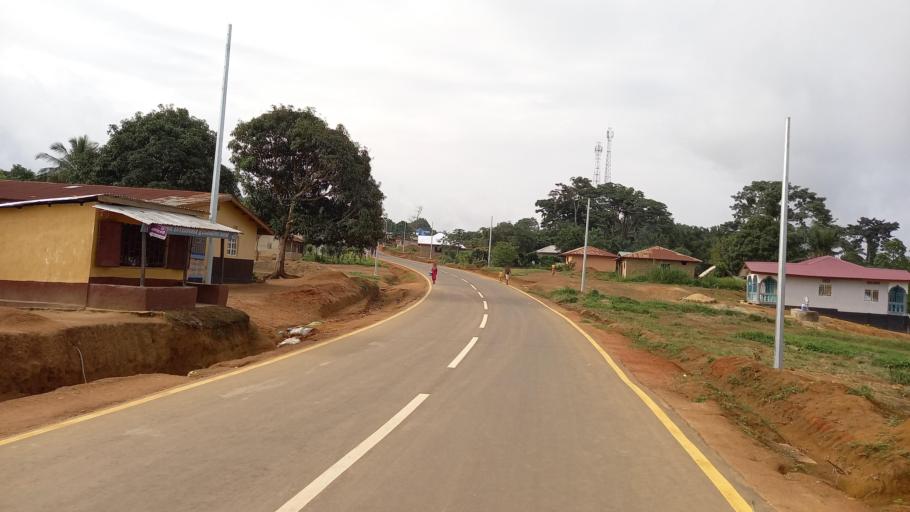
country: SL
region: Eastern Province
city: Kailahun
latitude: 8.2736
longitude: -10.5798
